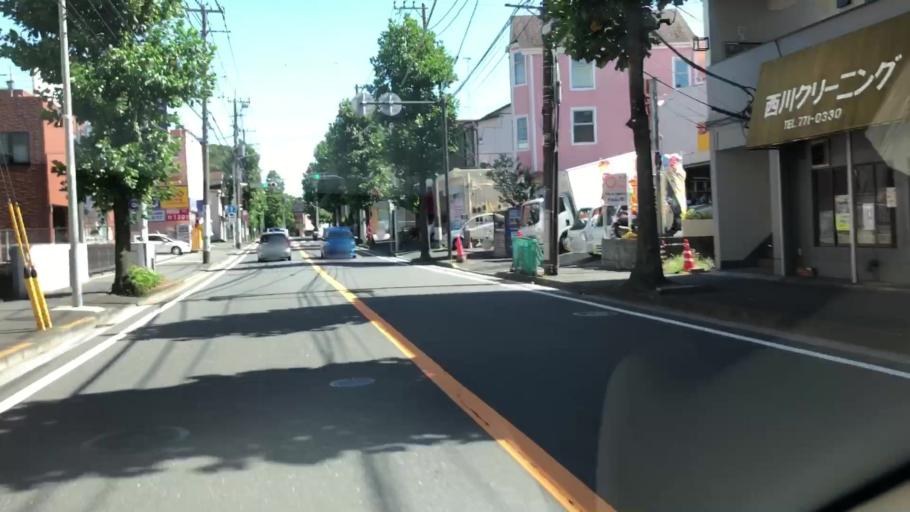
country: JP
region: Kanagawa
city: Yokohama
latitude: 35.3817
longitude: 139.6061
